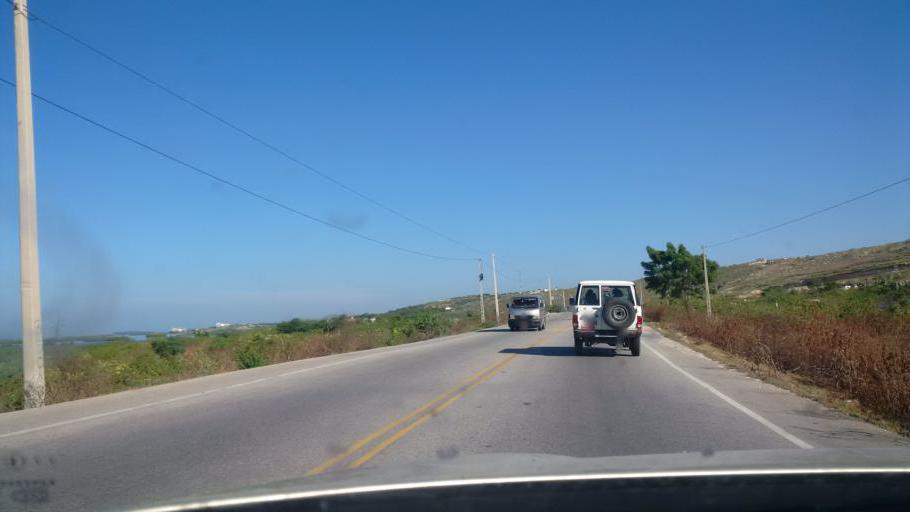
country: HT
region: Ouest
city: Cabaret
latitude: 18.6769
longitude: -72.3182
